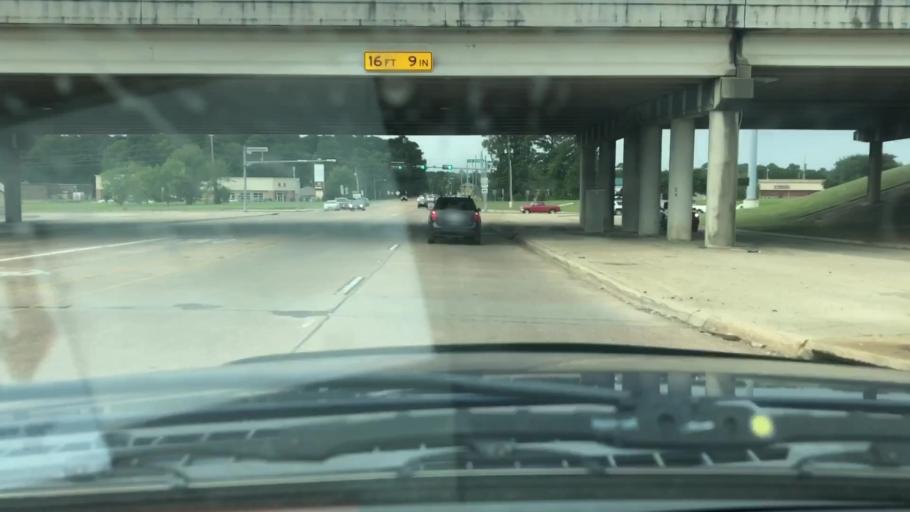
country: US
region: Texas
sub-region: Bowie County
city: Wake Village
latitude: 33.4435
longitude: -94.0964
